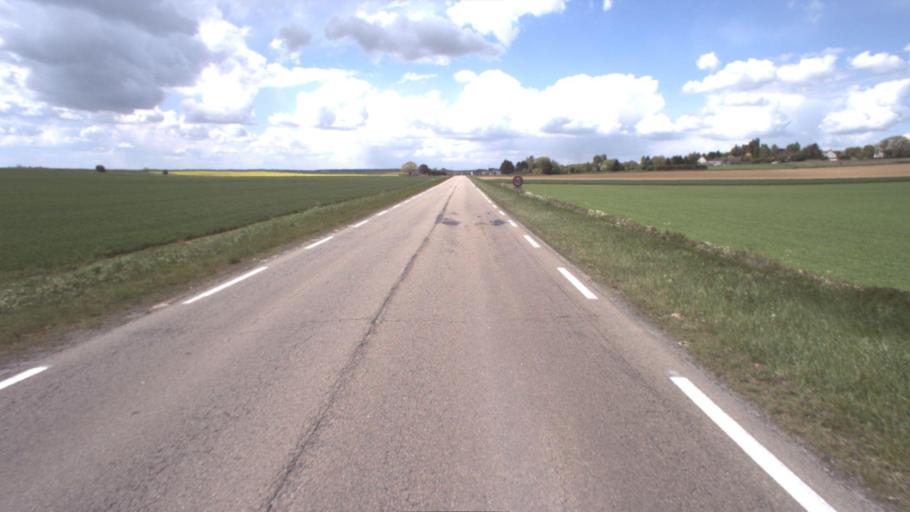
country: FR
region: Ile-de-France
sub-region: Departement de Seine-et-Marne
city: Villiers-Saint-Georges
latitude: 48.6921
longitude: 3.4044
